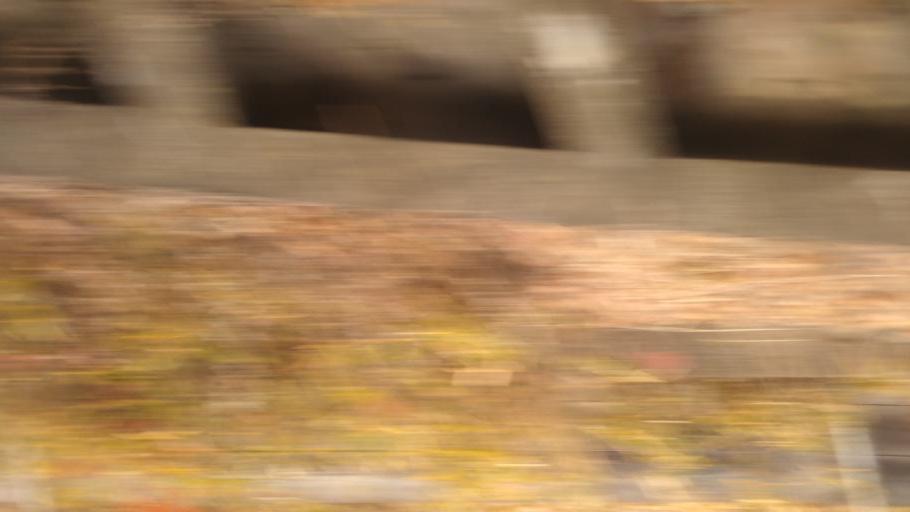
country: JP
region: Nagano
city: Nagano-shi
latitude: 36.5033
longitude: 138.0929
